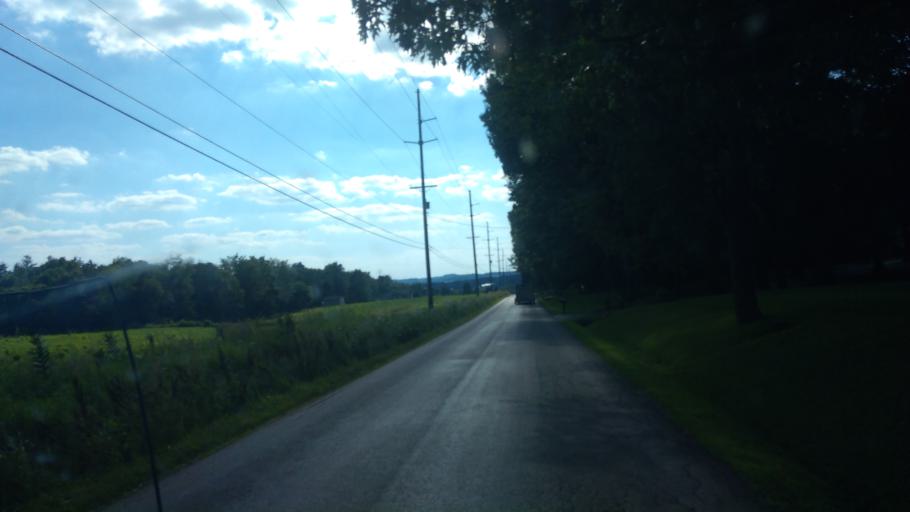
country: US
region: Ohio
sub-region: Wayne County
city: Shreve
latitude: 40.7116
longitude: -81.9495
